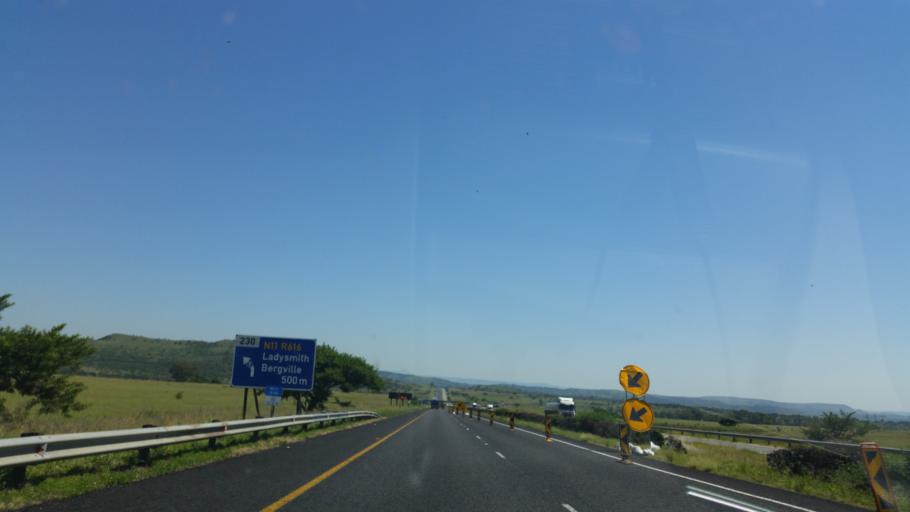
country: ZA
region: KwaZulu-Natal
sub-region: uThukela District Municipality
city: Ladysmith
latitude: -28.5975
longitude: 29.6100
